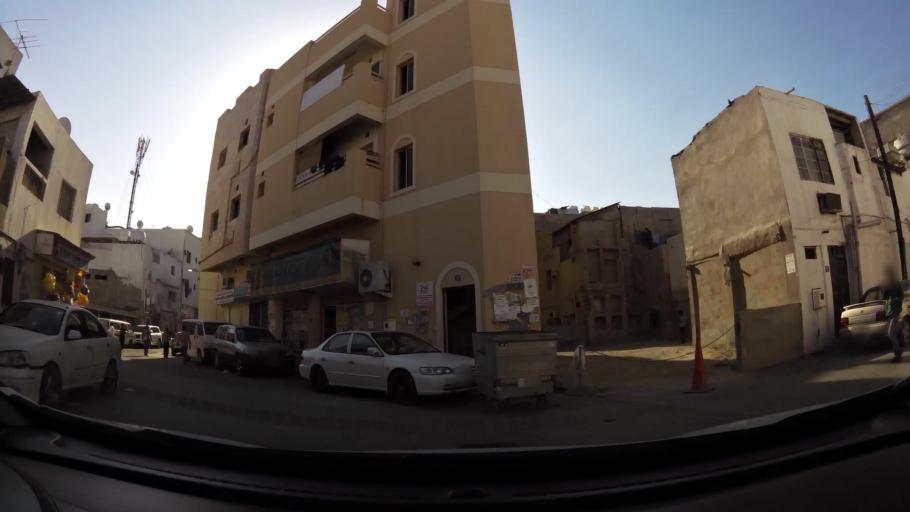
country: BH
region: Manama
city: Manama
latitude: 26.2272
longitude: 50.5757
